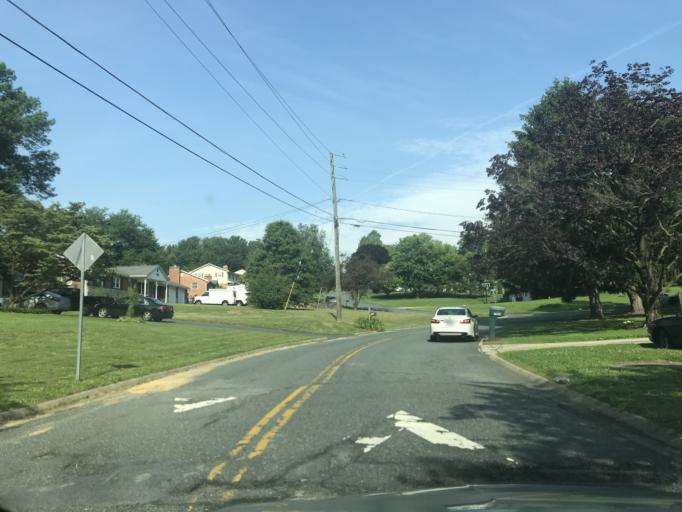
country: US
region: Maryland
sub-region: Harford County
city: Bel Air North
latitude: 39.5570
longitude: -76.3927
